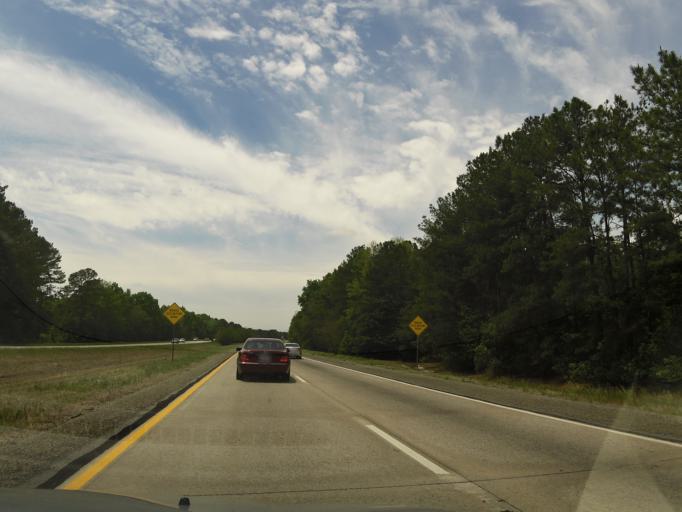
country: US
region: Georgia
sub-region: Bryan County
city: Pembroke
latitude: 32.2390
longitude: -81.6759
